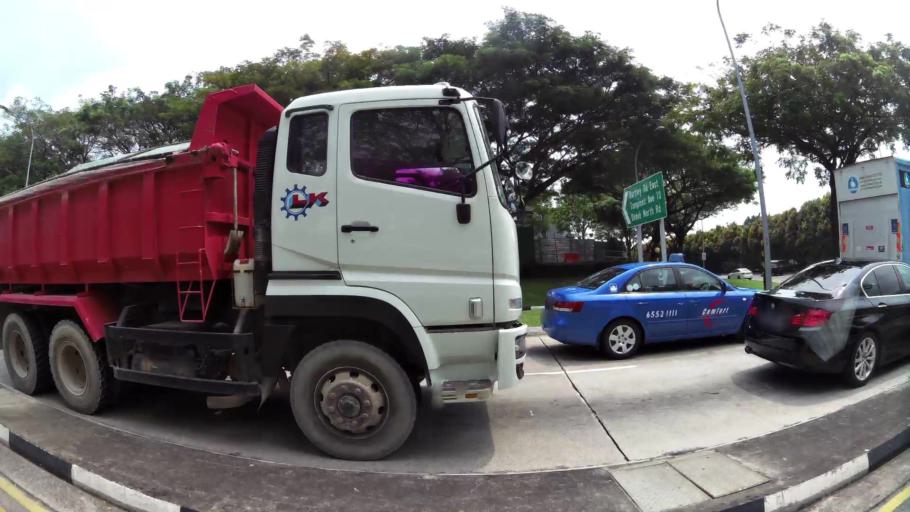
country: SG
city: Singapore
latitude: 1.3407
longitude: 103.8982
